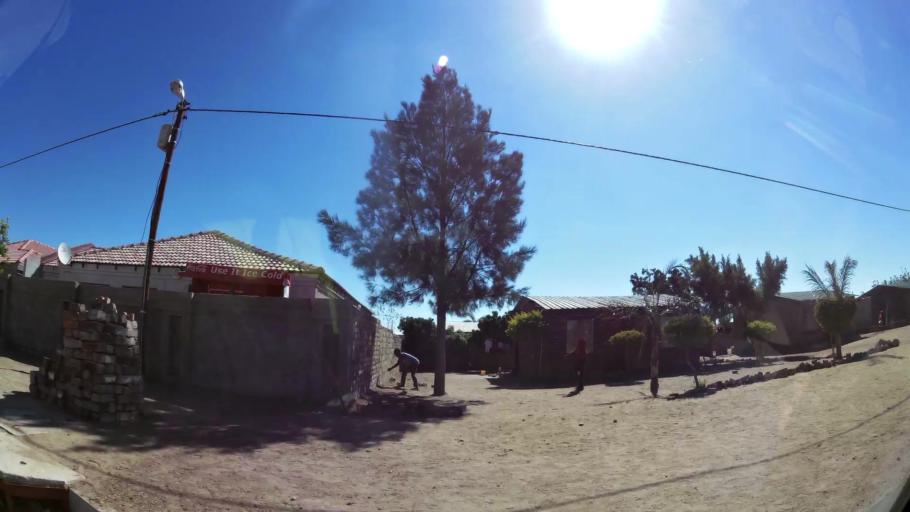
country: ZA
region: Limpopo
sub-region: Capricorn District Municipality
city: Polokwane
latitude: -23.8508
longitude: 29.4134
